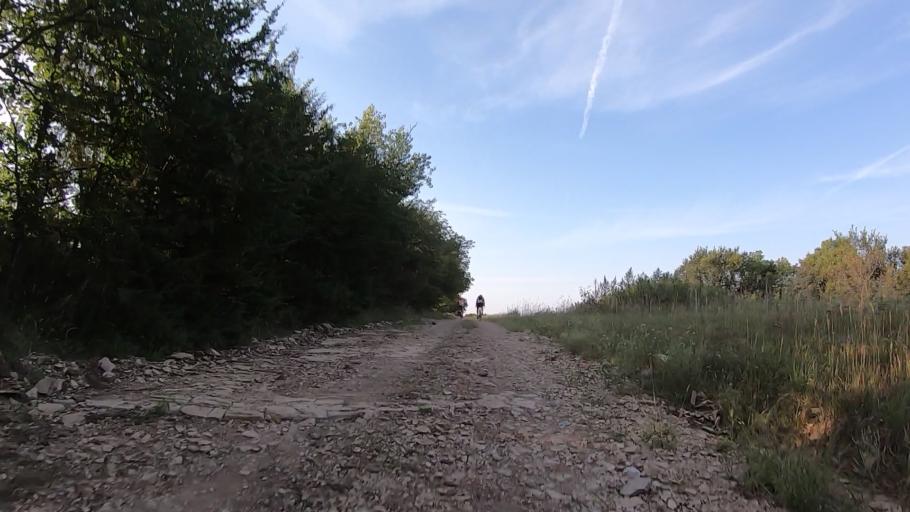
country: US
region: Kansas
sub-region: Marshall County
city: Blue Rapids
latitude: 39.7604
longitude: -96.7507
